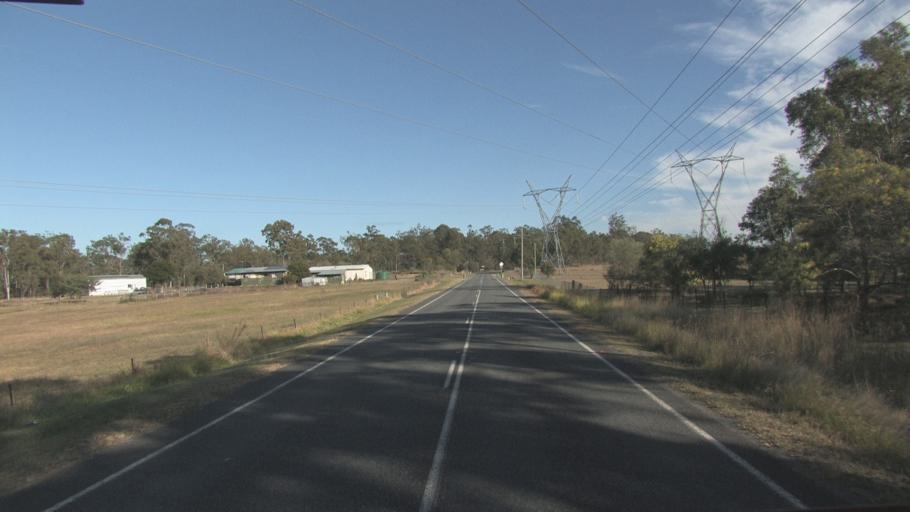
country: AU
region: Queensland
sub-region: Logan
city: North Maclean
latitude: -27.7528
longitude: 152.9981
